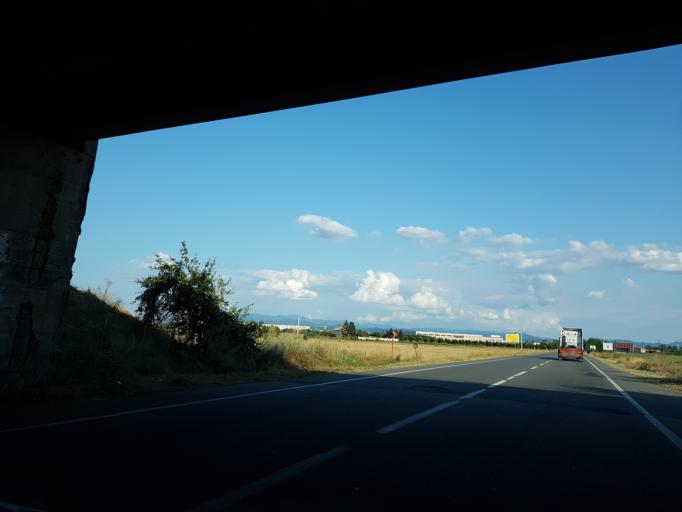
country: IT
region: Piedmont
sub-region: Provincia di Alessandria
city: Pozzolo Formigaro
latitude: 44.8095
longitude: 8.7658
